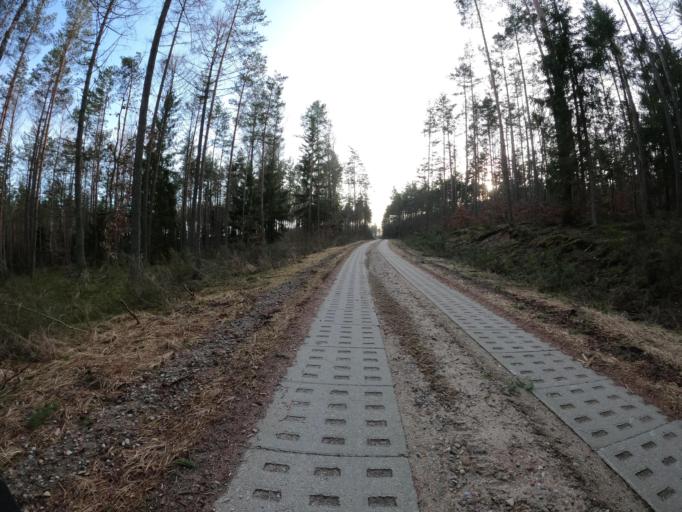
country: PL
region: West Pomeranian Voivodeship
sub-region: Powiat koszalinski
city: Polanow
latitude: 54.1424
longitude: 16.6713
